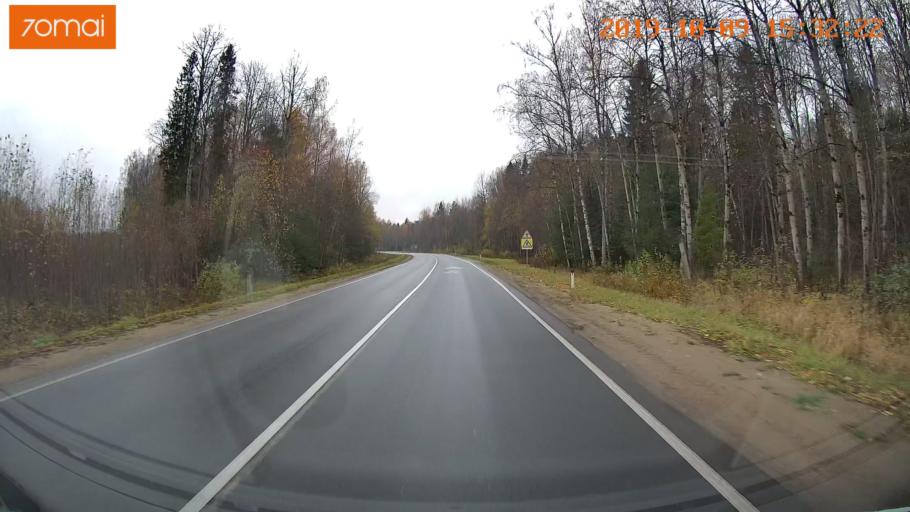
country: RU
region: Kostroma
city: Oktyabr'skiy
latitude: 57.9652
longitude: 41.2786
